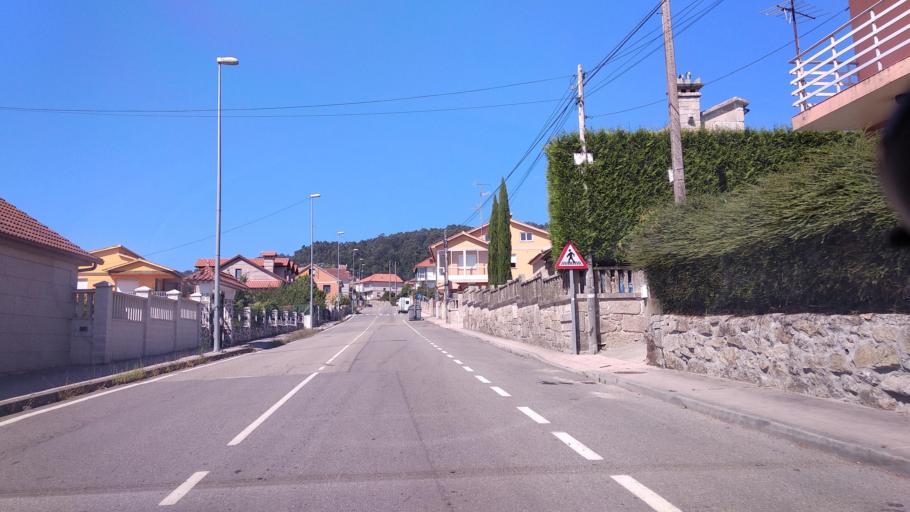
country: ES
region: Galicia
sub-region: Provincia de Pontevedra
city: Cangas
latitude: 42.2735
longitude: -8.7676
